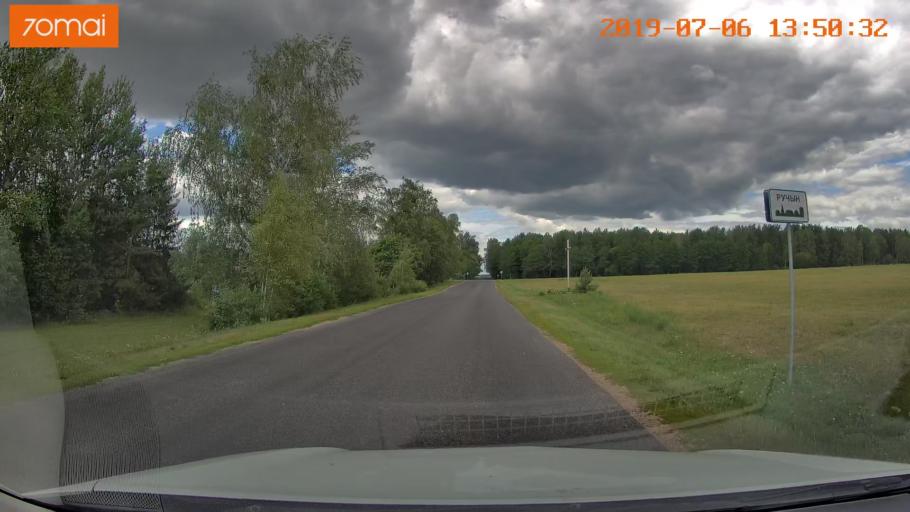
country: BY
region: Minsk
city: Ivyanyets
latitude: 53.7005
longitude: 26.8425
